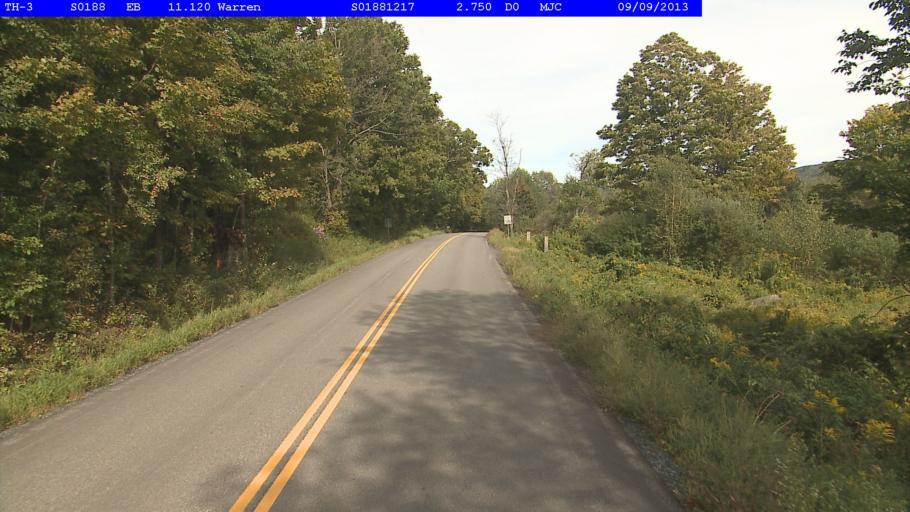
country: US
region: Vermont
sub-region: Addison County
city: Bristol
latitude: 44.1035
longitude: -72.8779
